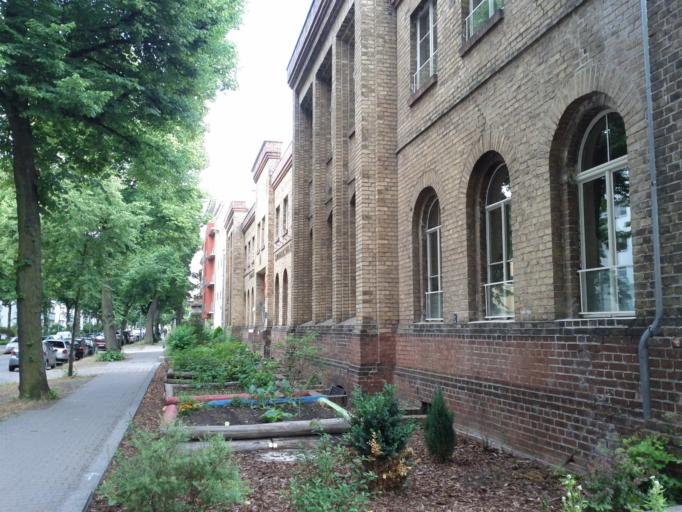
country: DE
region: Berlin
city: Friedrichshagen
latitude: 52.4531
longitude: 13.6208
